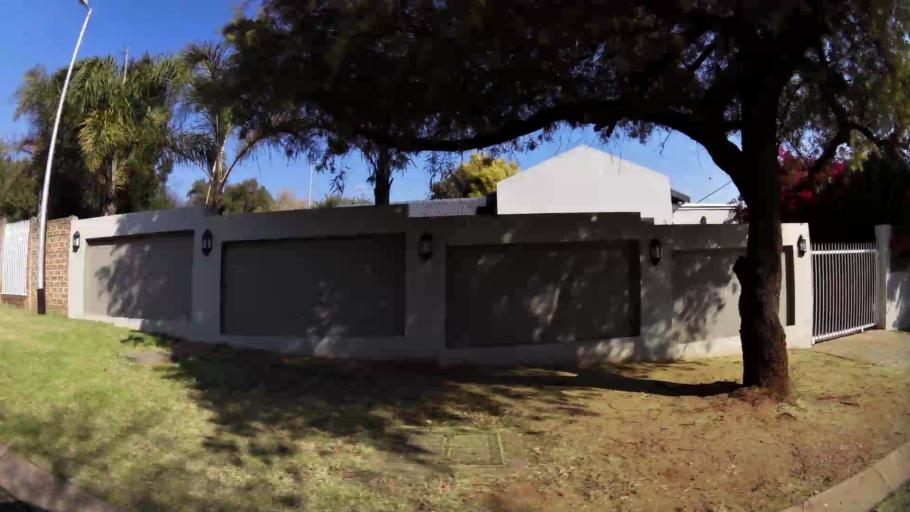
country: ZA
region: Gauteng
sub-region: City of Johannesburg Metropolitan Municipality
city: Modderfontein
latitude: -26.1073
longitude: 28.1533
